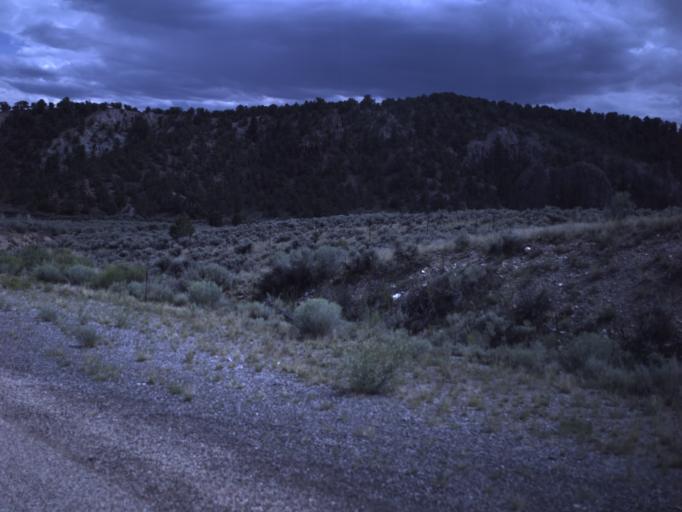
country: US
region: Utah
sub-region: Garfield County
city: Panguitch
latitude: 37.9708
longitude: -112.4445
